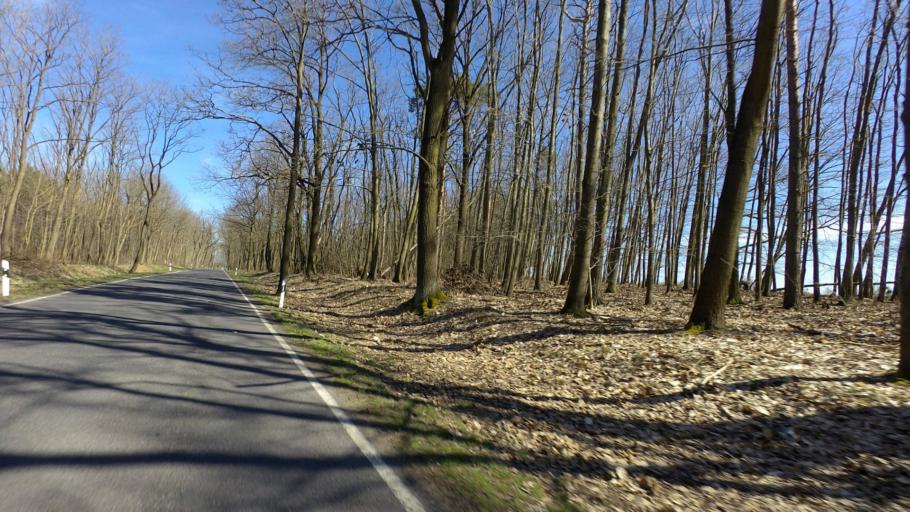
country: DE
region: Brandenburg
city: Munchehofe
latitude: 52.1562
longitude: 13.8612
